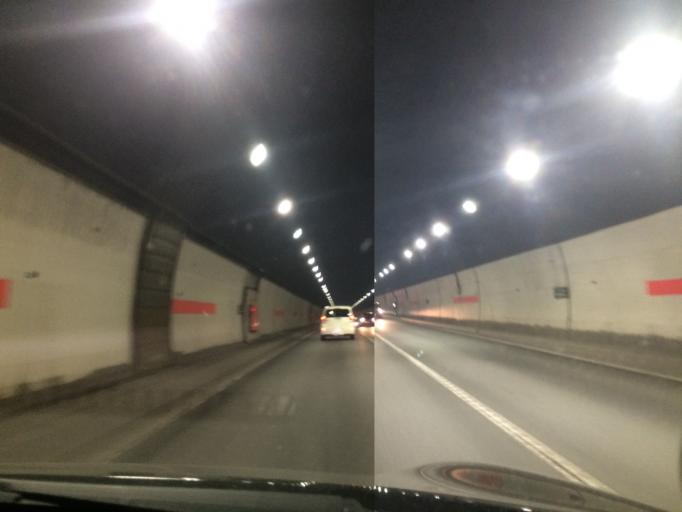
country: JP
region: Hokkaido
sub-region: Asahikawa-shi
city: Asahikawa
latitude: 43.7394
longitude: 142.2430
